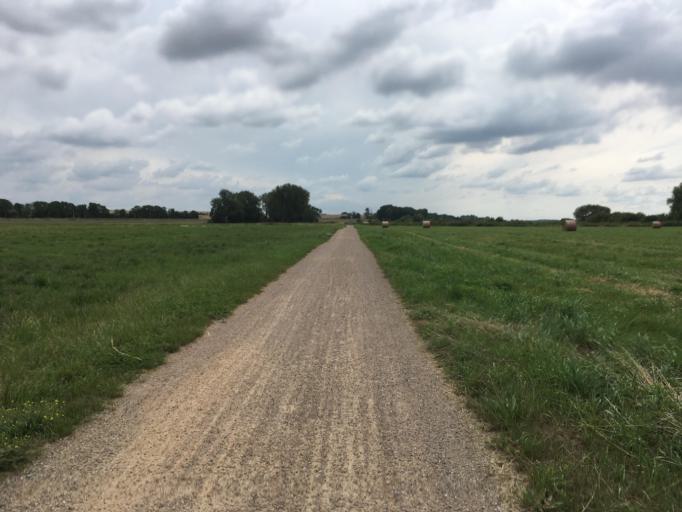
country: DE
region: Brandenburg
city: Prenzlau
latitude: 53.2782
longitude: 13.8806
